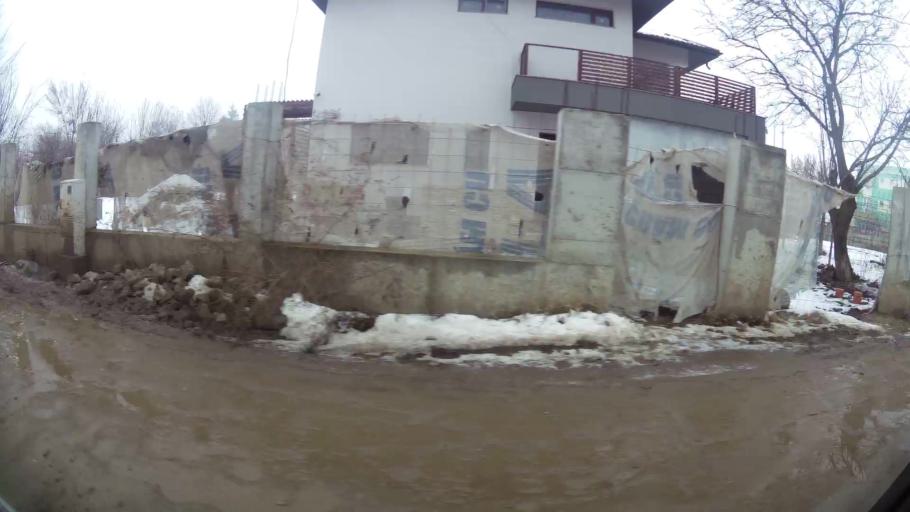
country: RO
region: Ilfov
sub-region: Comuna Chiajna
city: Rosu
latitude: 44.4479
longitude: 26.0208
